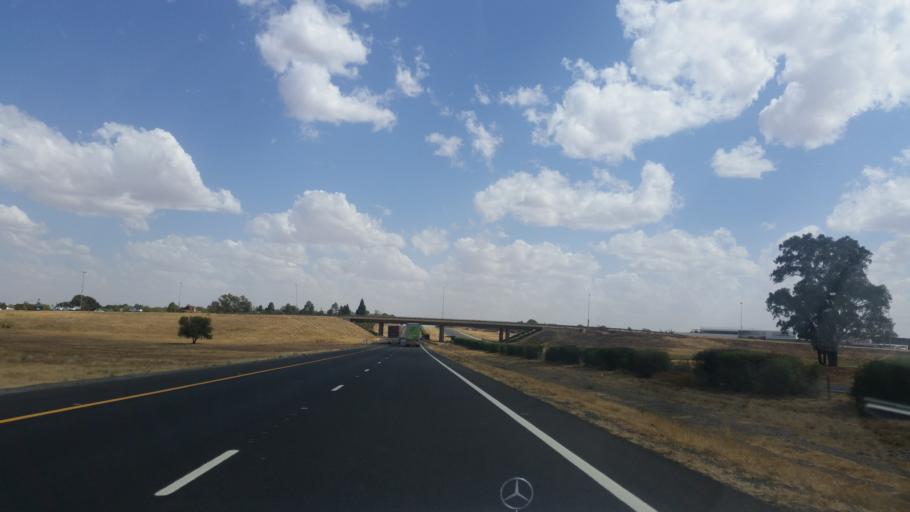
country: ZA
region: Orange Free State
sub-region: Mangaung Metropolitan Municipality
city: Bloemfontein
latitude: -29.0884
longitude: 26.1726
